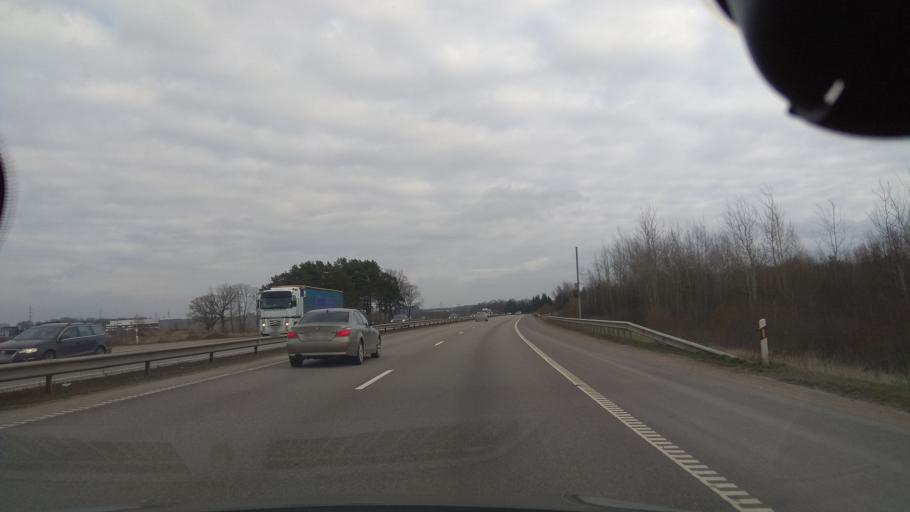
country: LT
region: Kauno apskritis
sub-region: Kaunas
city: Silainiai
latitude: 54.9280
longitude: 23.8544
